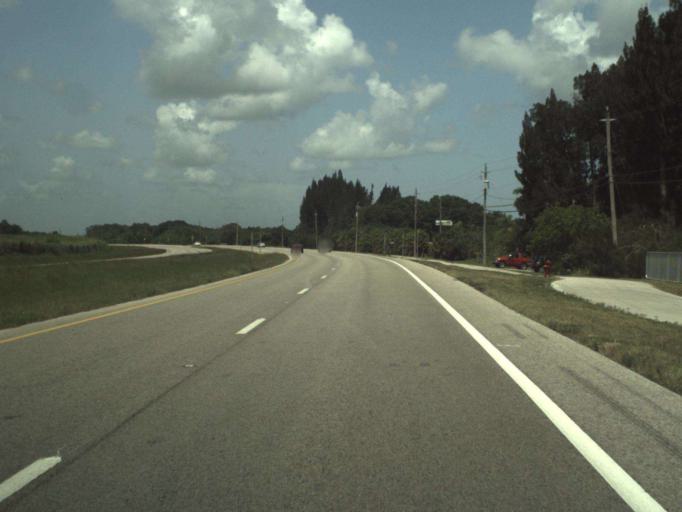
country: US
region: Florida
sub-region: Saint Lucie County
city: Fort Pierce South
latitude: 27.4113
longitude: -80.4132
